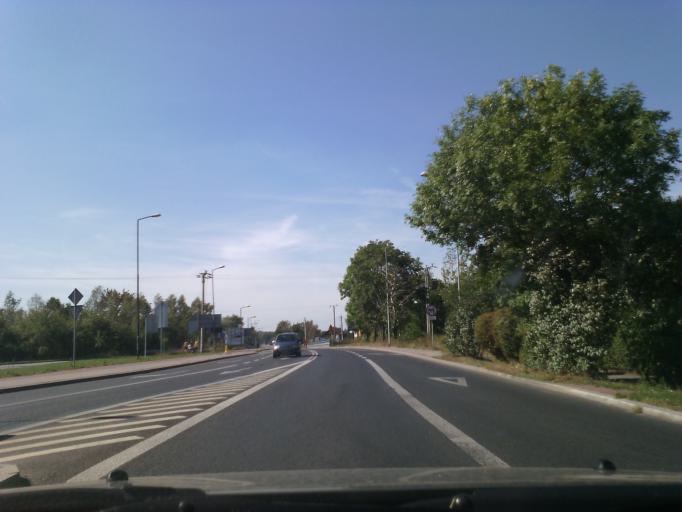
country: PL
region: Silesian Voivodeship
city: Zebrzydowice
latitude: 50.0919
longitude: 18.5179
